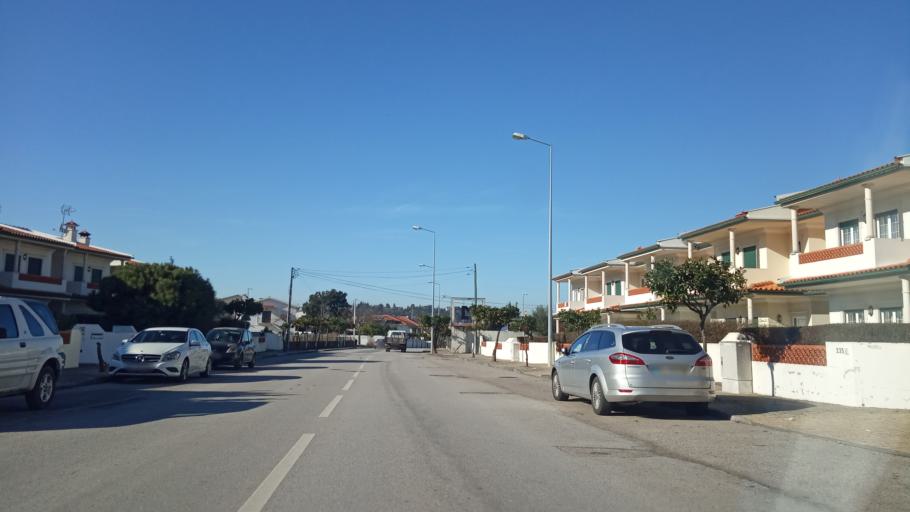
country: PT
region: Aveiro
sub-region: Anadia
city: Anadia
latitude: 40.4357
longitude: -8.4297
